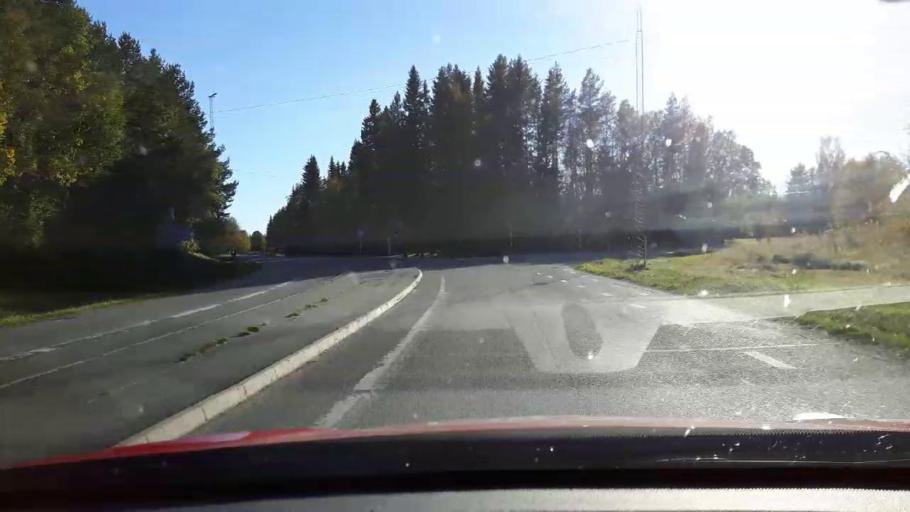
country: SE
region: Jaemtland
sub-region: Stroemsunds Kommun
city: Stroemsund
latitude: 63.8425
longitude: 15.5263
